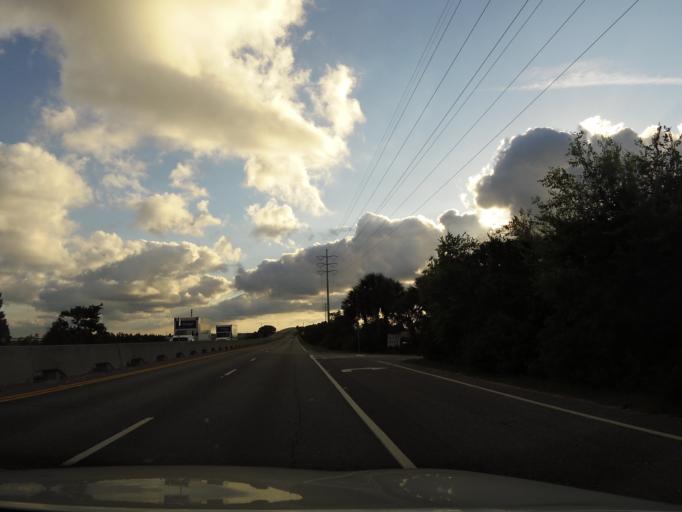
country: US
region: Georgia
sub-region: Glynn County
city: Saint Simon Mills
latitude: 31.1681
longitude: -81.4384
